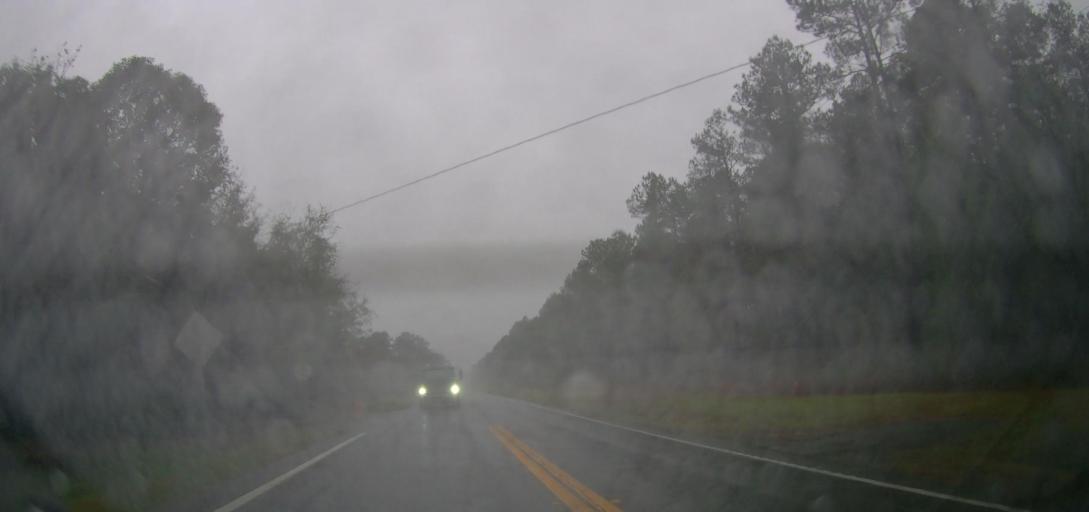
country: US
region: Georgia
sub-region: Jones County
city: Gray
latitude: 33.1603
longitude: -83.4449
